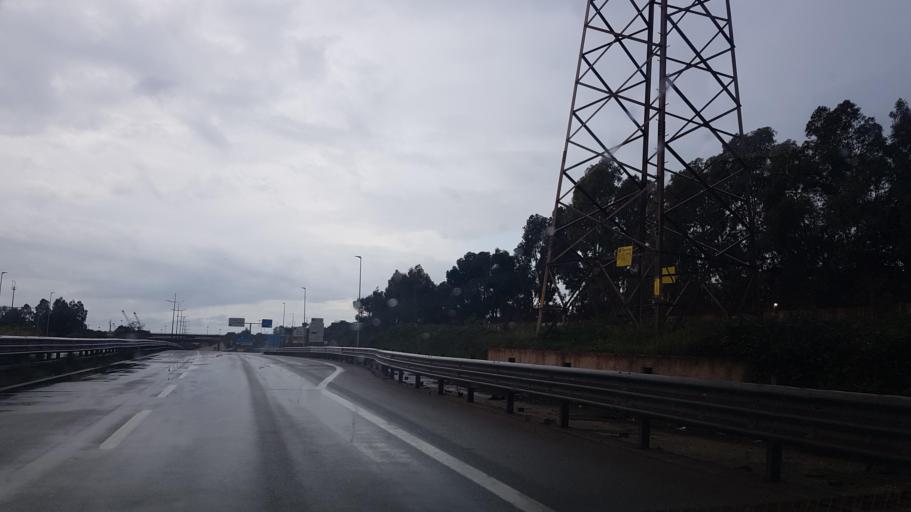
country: IT
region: Apulia
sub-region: Provincia di Taranto
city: Statte
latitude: 40.4878
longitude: 17.2080
